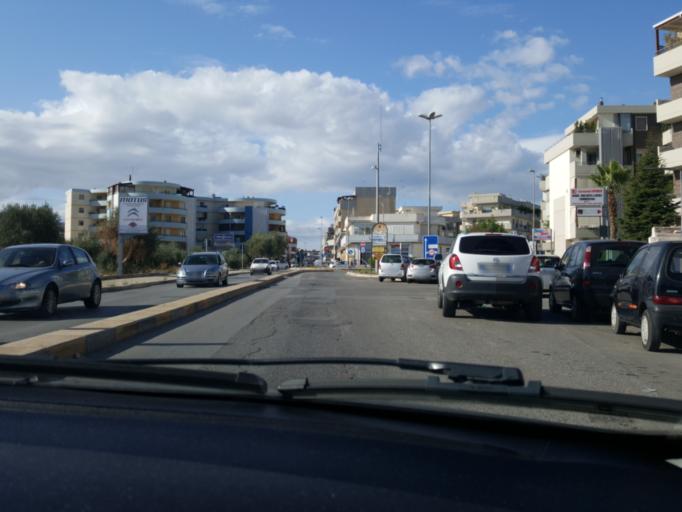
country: IT
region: Apulia
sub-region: Provincia di Bari
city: Triggiano
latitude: 41.0708
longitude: 16.9350
